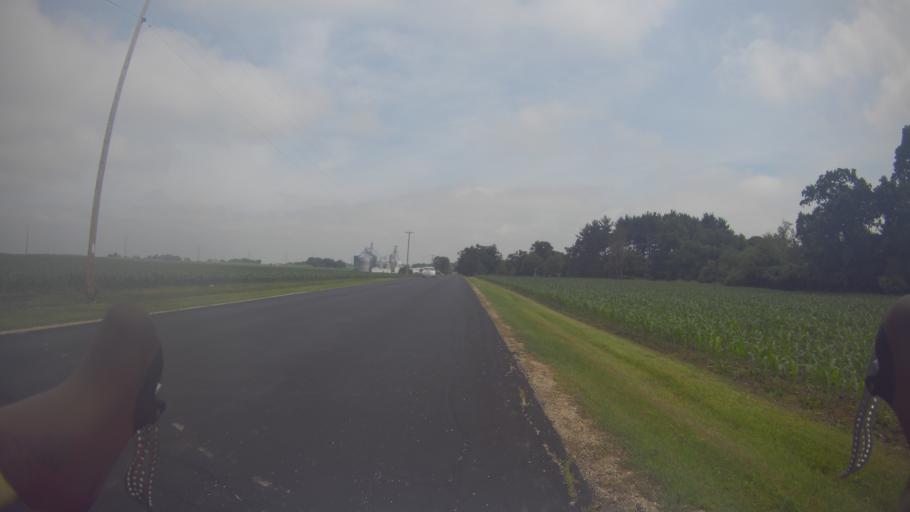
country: US
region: Wisconsin
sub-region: Rock County
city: Edgerton
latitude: 42.8857
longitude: -89.0395
